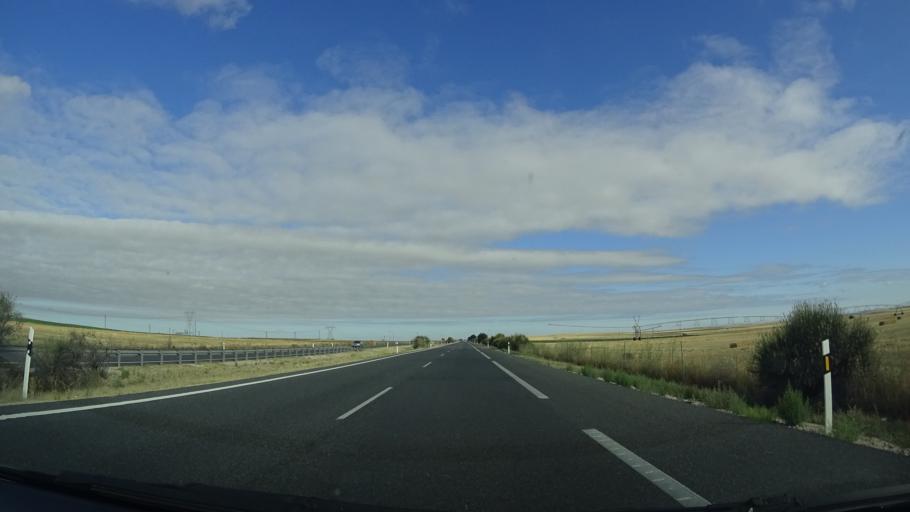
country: ES
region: Castille and Leon
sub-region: Provincia de Valladolid
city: Ataquines
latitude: 41.1926
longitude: -4.8145
